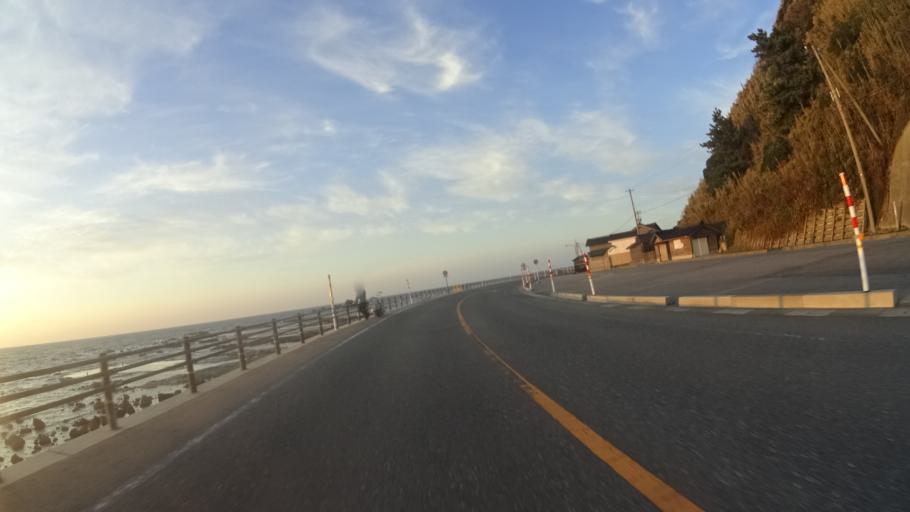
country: JP
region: Ishikawa
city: Nanao
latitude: 37.2367
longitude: 136.7008
